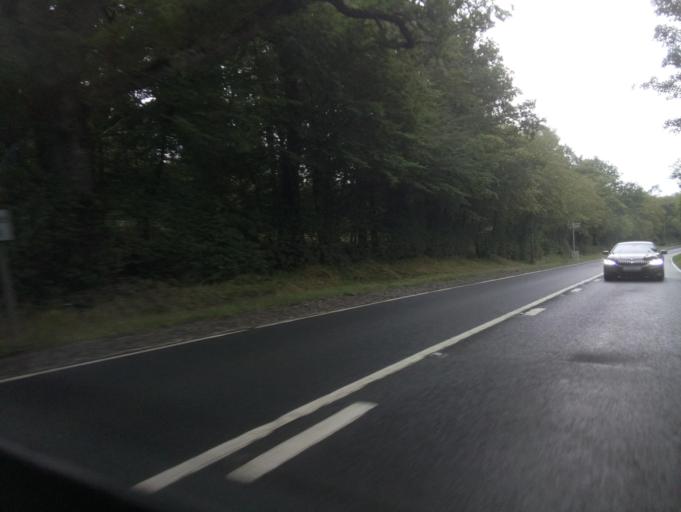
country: GB
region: Scotland
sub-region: Dumfries and Galloway
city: Lochmaben
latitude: 55.2301
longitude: -3.4618
